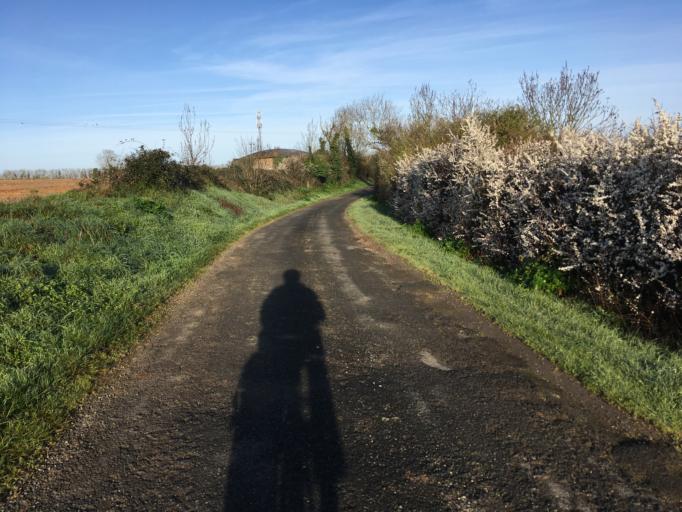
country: FR
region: Poitou-Charentes
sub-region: Departement de la Charente-Maritime
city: Nieul-sur-Mer
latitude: 46.1977
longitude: -1.1783
